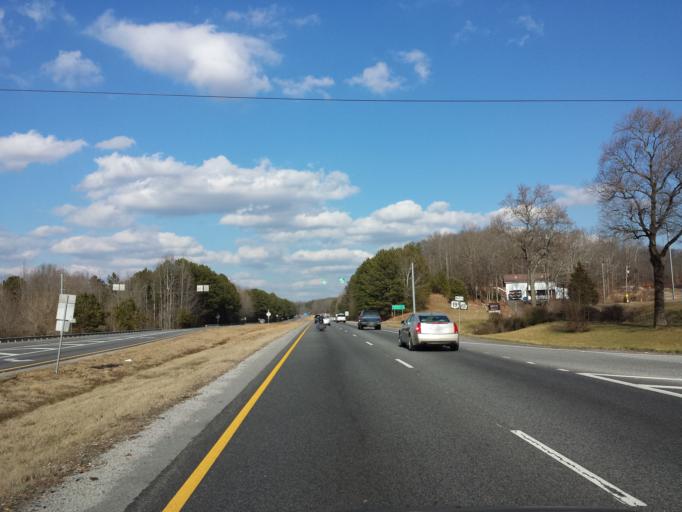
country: US
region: Georgia
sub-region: Forsyth County
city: Cumming
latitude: 34.2636
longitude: -84.0866
